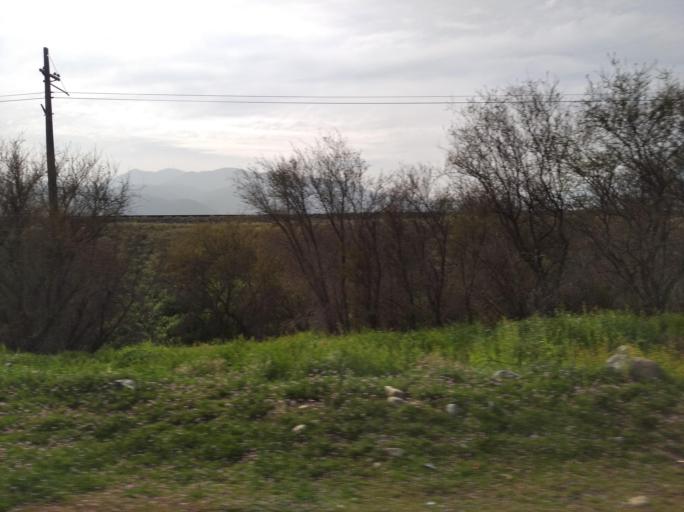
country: CL
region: Santiago Metropolitan
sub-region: Provincia de Chacabuco
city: Lampa
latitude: -33.1247
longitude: -70.9237
